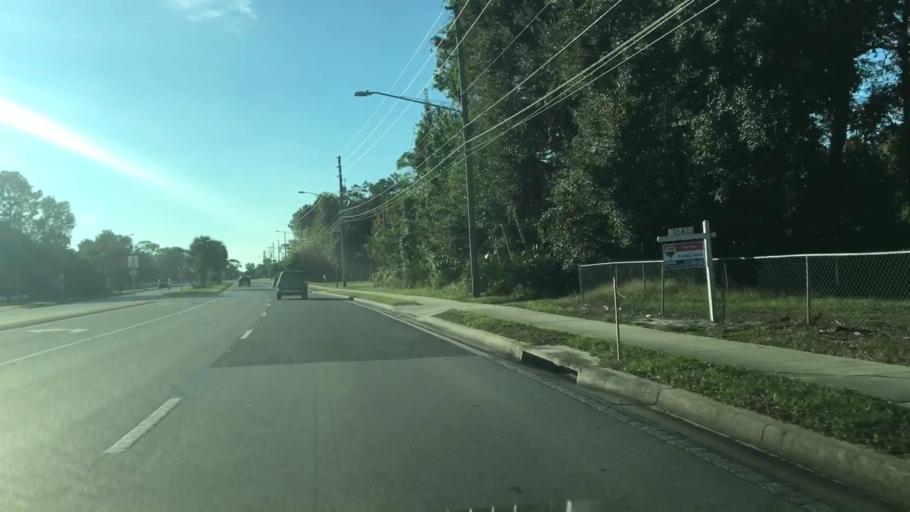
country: US
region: Florida
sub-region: Orange County
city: Azalea Park
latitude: 28.5113
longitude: -81.2889
